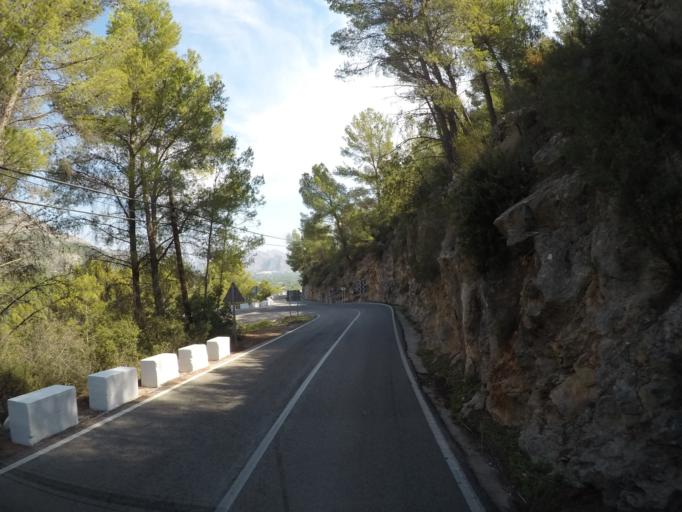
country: ES
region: Valencia
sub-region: Provincia de Alicante
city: Tormos
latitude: 38.7844
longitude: -0.0863
